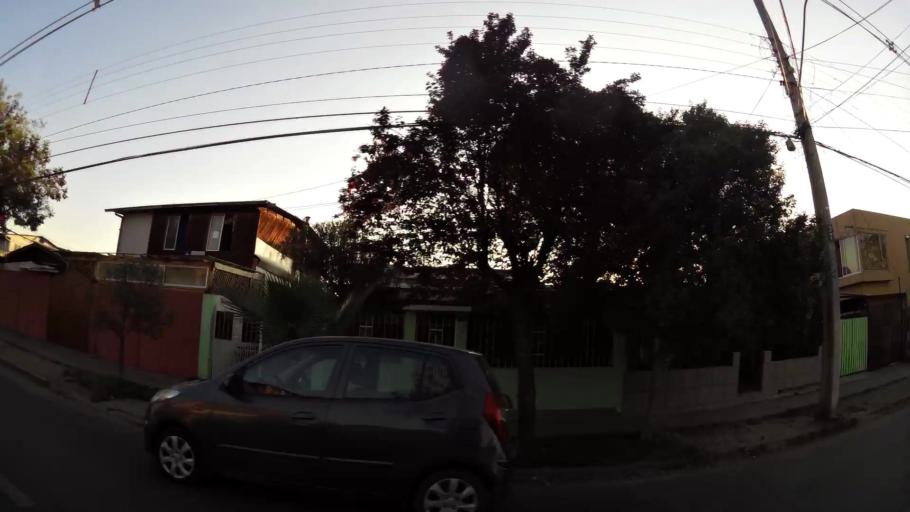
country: CL
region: Santiago Metropolitan
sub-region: Provincia de Santiago
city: Santiago
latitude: -33.5087
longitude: -70.6287
